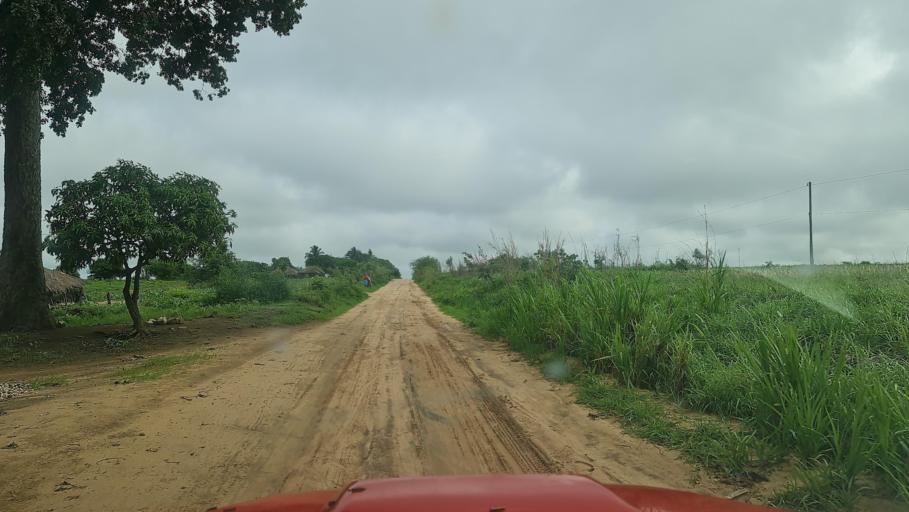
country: MW
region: Southern Region
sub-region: Nsanje District
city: Nsanje
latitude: -17.1995
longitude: 35.6998
